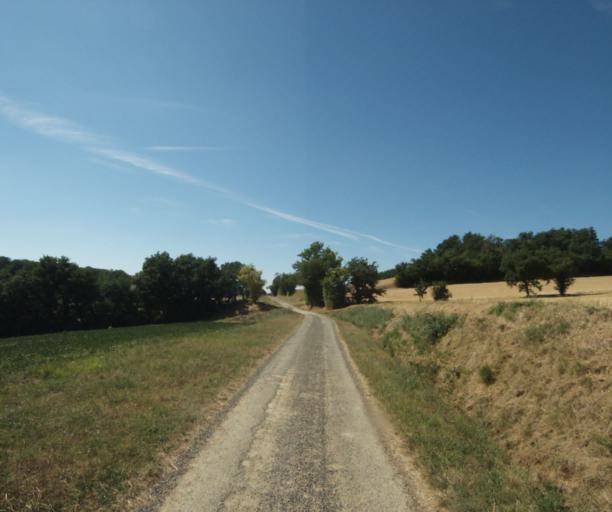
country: FR
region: Midi-Pyrenees
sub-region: Departement de la Haute-Garonne
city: Saint-Felix-Lauragais
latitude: 43.4987
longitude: 1.9328
